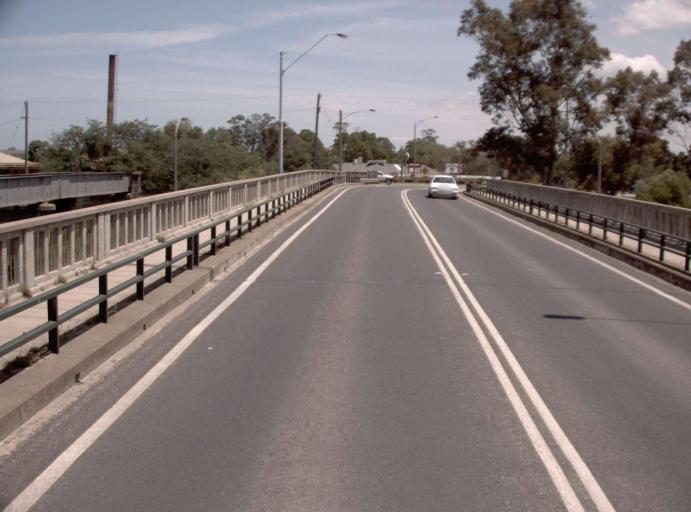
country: AU
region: Victoria
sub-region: East Gippsland
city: Bairnsdale
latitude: -37.8252
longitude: 147.6412
